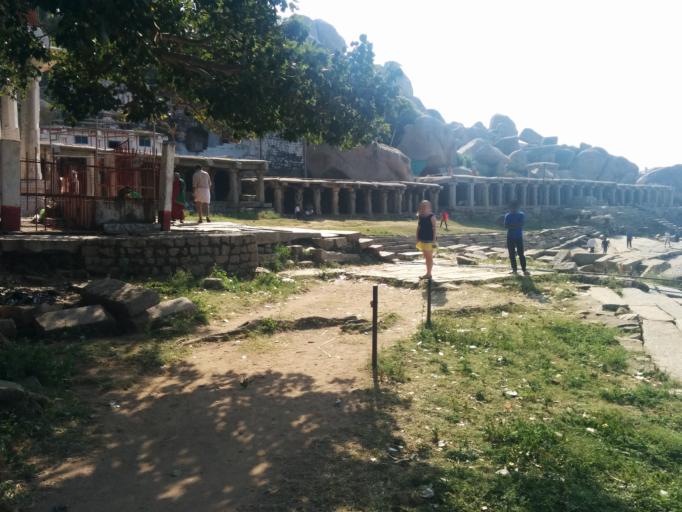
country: IN
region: Karnataka
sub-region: Bellary
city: Hampi
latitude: 15.3362
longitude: 76.4684
